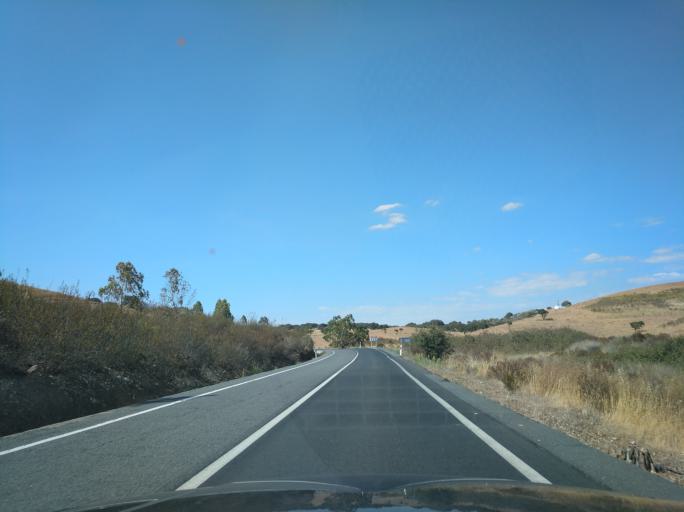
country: ES
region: Andalusia
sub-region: Provincia de Huelva
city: Alosno
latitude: 37.5139
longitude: -7.1319
